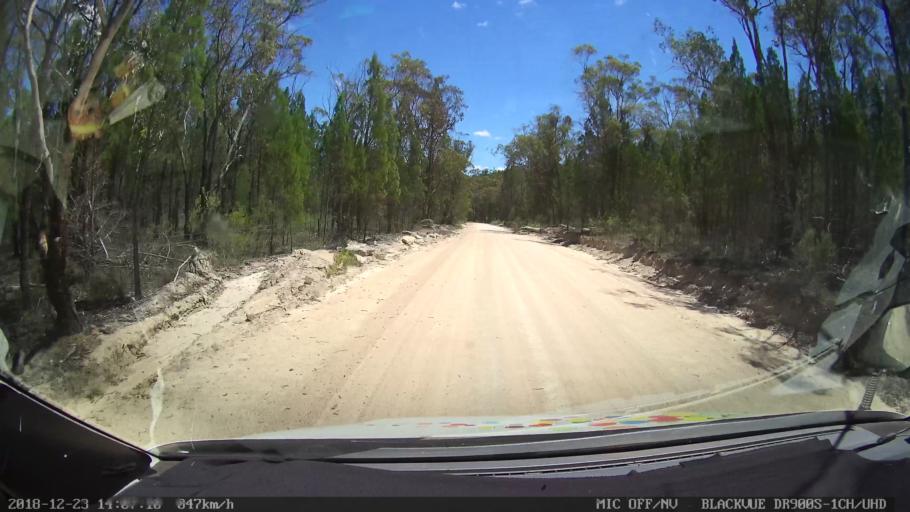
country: AU
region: New South Wales
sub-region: Tamworth Municipality
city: Manilla
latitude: -30.6343
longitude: 151.0729
